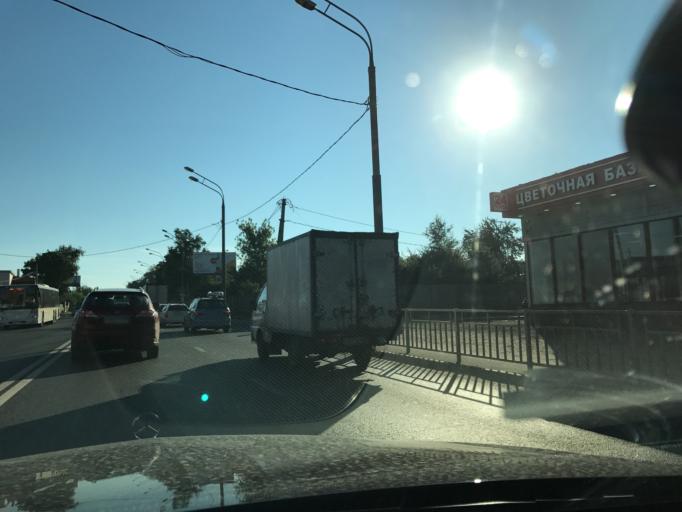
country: RU
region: Moscow
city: Vostochnyy
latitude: 55.8153
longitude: 37.8445
